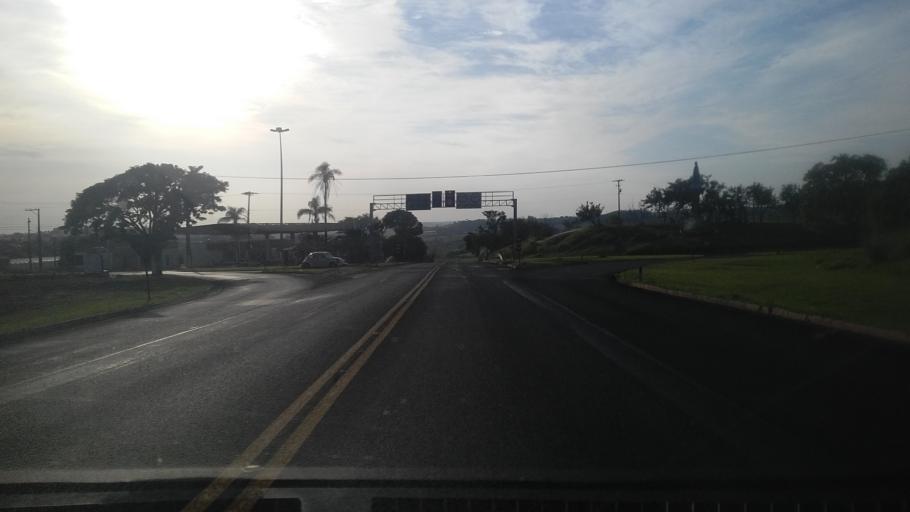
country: BR
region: Parana
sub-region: Bandeirantes
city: Bandeirantes
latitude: -23.1512
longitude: -50.5254
